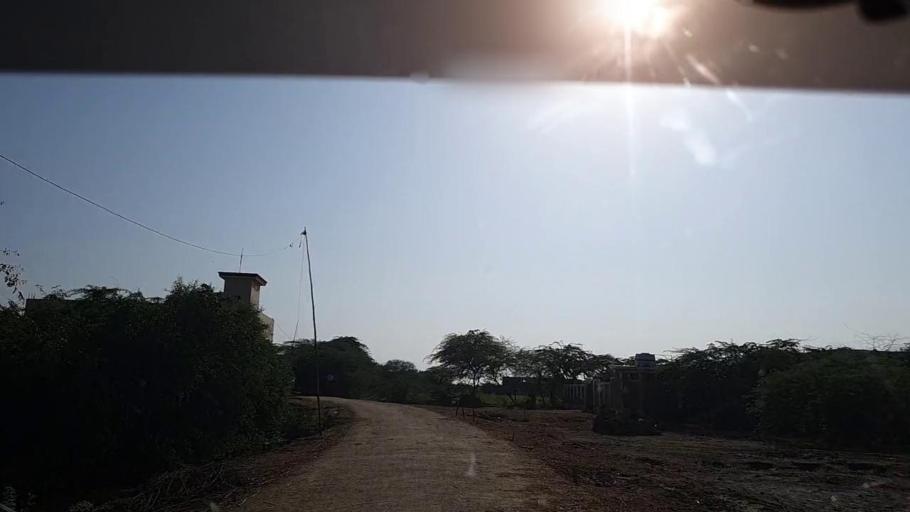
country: PK
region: Sindh
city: Badin
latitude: 24.6897
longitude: 68.8397
